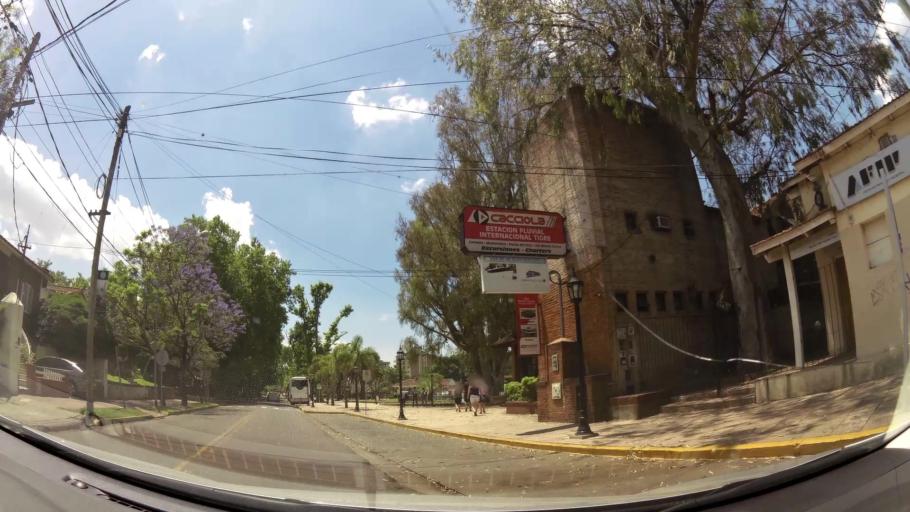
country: AR
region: Buenos Aires
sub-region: Partido de Tigre
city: Tigre
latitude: -34.4212
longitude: -58.5812
